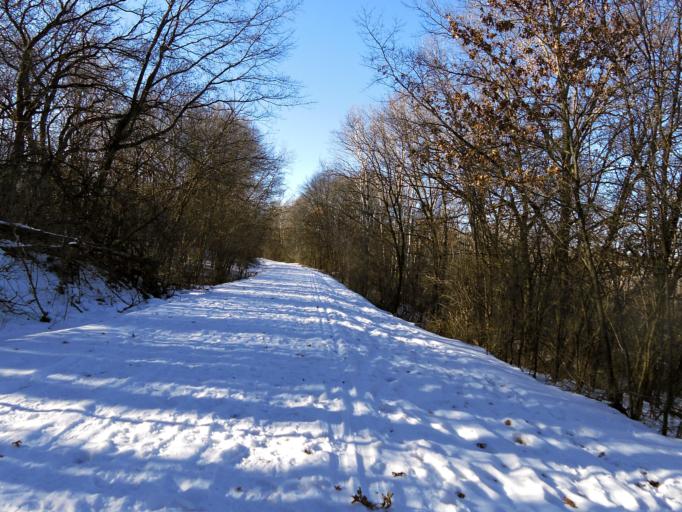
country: US
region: Minnesota
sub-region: Washington County
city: Grant
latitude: 45.0766
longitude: -92.8767
